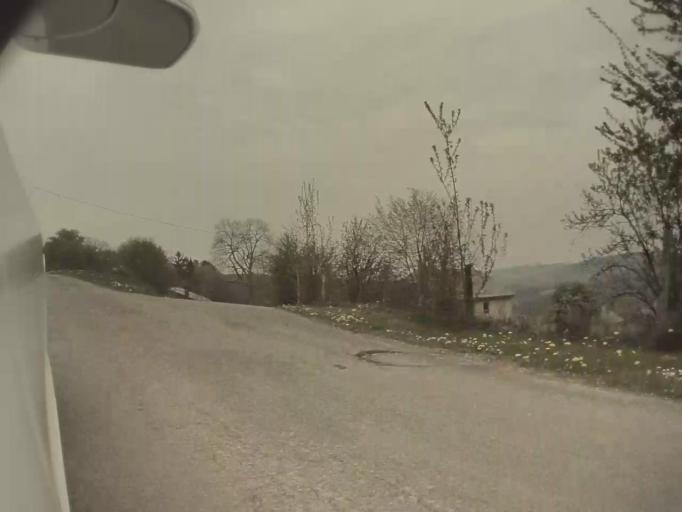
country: BE
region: Wallonia
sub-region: Province du Luxembourg
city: La Roche-en-Ardenne
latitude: 50.2345
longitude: 5.6202
